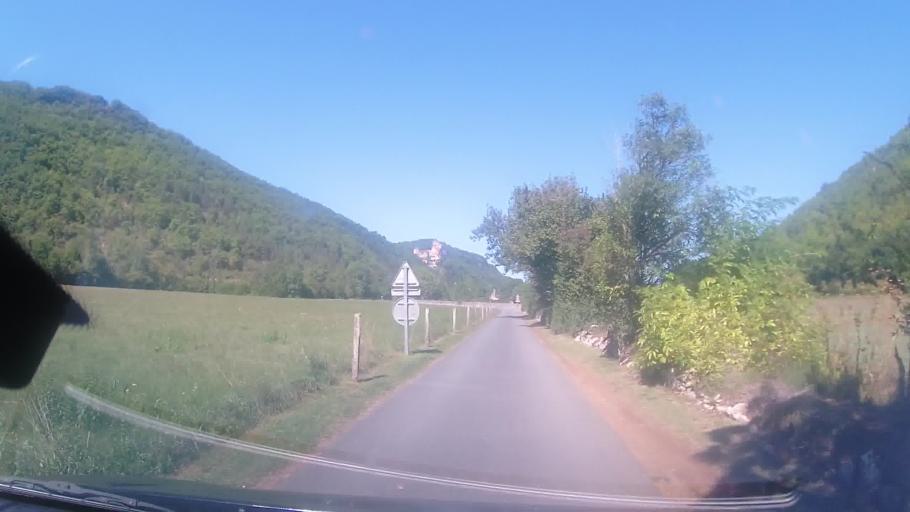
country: FR
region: Aquitaine
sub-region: Departement de la Dordogne
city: Cenac-et-Saint-Julien
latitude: 44.8062
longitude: 1.1575
